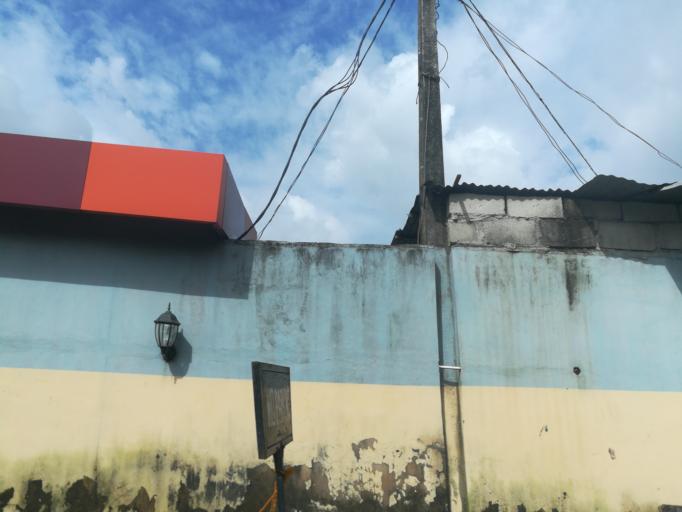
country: NG
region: Lagos
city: Somolu
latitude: 6.5491
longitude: 3.3715
